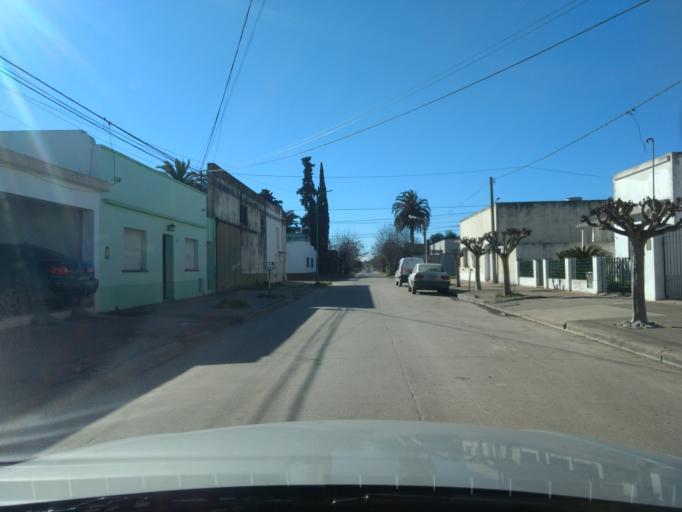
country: AR
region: Buenos Aires
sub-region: Partido de Navarro
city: Navarro
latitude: -35.0016
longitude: -59.2769
